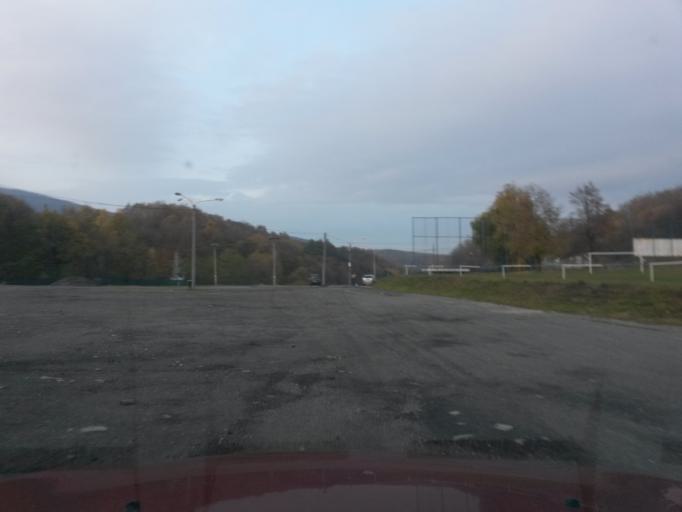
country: SK
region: Kosicky
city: Kosice
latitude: 48.7797
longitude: 21.2022
